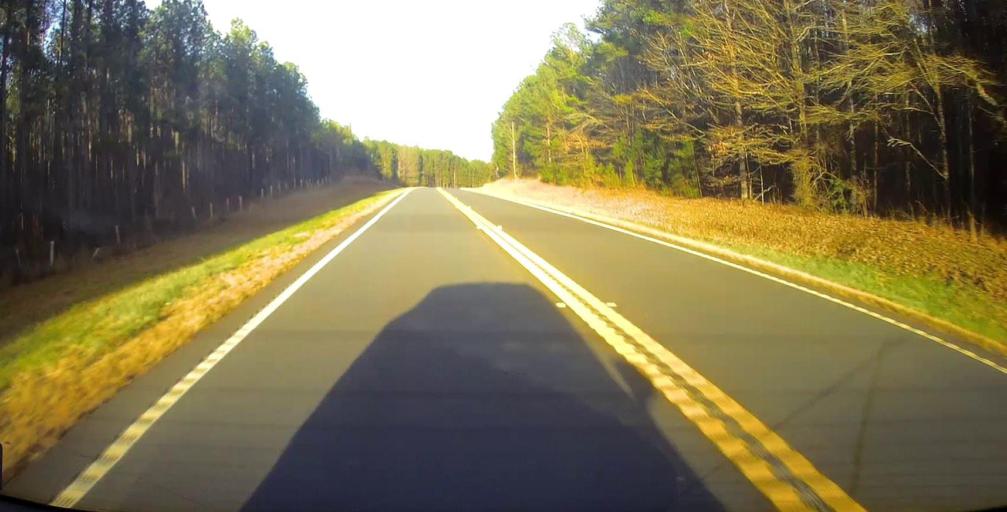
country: US
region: Georgia
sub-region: Talbot County
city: Sardis
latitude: 32.7466
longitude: -84.5923
